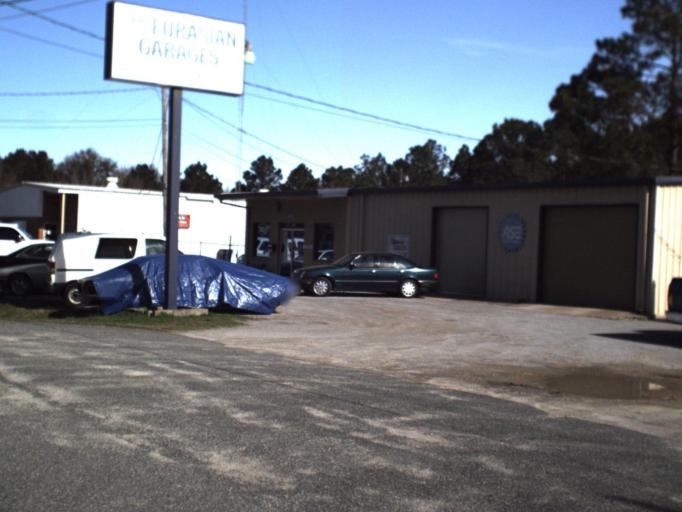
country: US
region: Florida
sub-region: Bay County
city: Panama City
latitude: 30.1842
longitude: -85.6696
